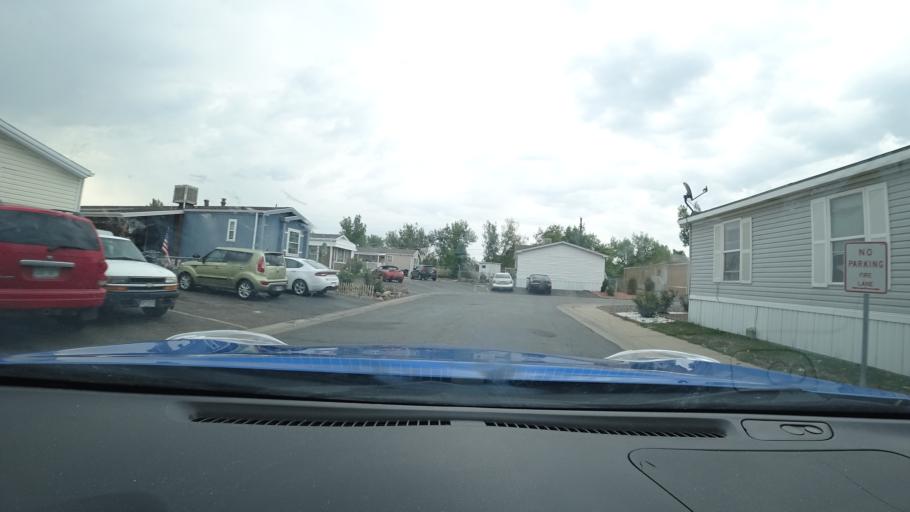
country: US
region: Colorado
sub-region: Adams County
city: Aurora
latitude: 39.7414
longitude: -104.7828
